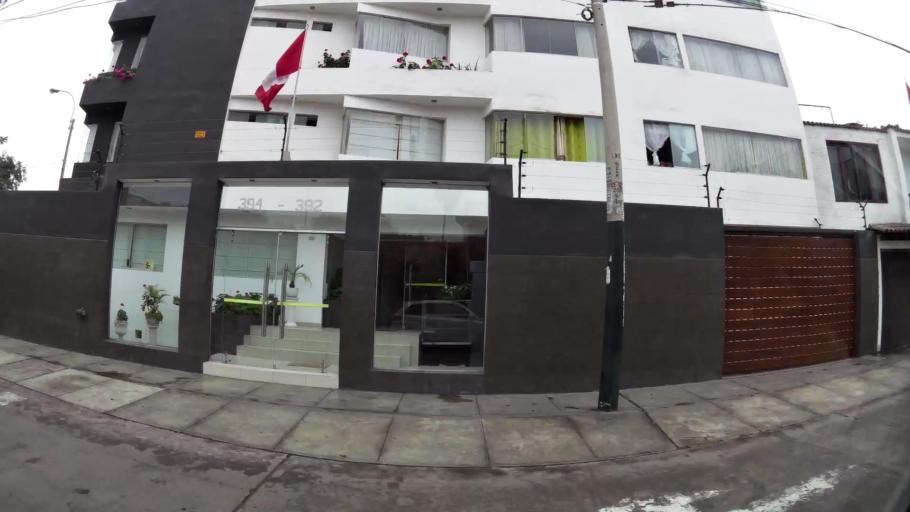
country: PE
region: Lima
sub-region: Lima
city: Surco
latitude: -12.1315
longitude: -77.0028
